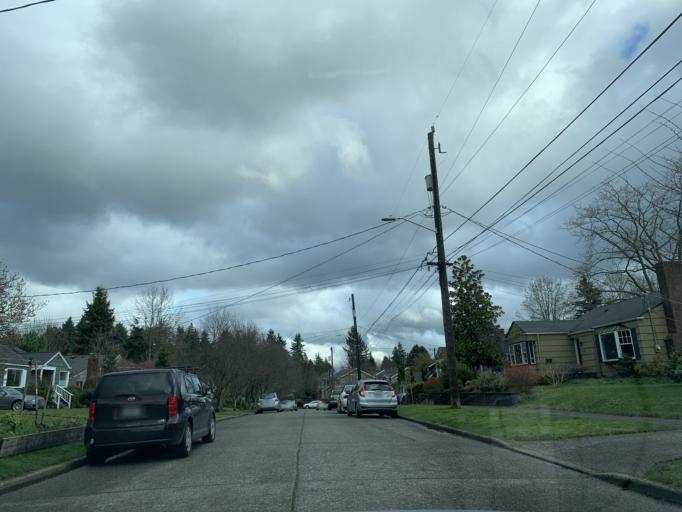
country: US
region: Washington
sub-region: King County
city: Yarrow Point
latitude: 47.6694
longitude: -122.2811
